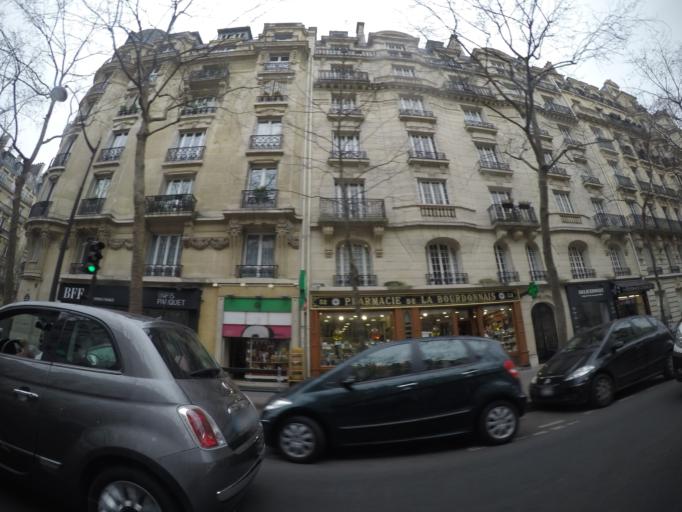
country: FR
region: Ile-de-France
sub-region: Departement des Hauts-de-Seine
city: Vanves
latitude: 48.8565
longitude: 2.3021
